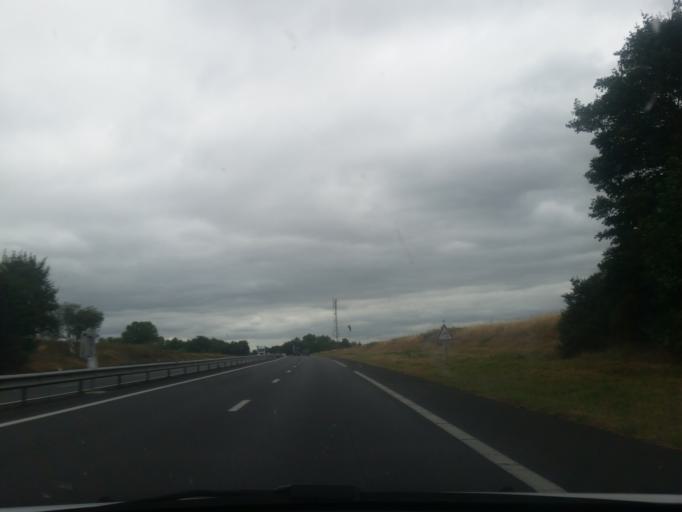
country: FR
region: Pays de la Loire
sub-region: Departement de la Sarthe
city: Noyen-sur-Sarthe
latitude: 47.8503
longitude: -0.1218
